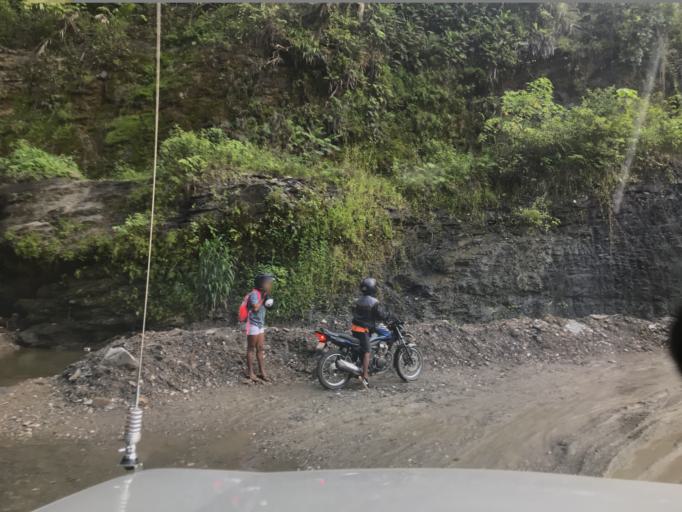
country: TL
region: Aileu
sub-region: Aileu Villa
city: Aileu
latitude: -8.6454
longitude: 125.5249
